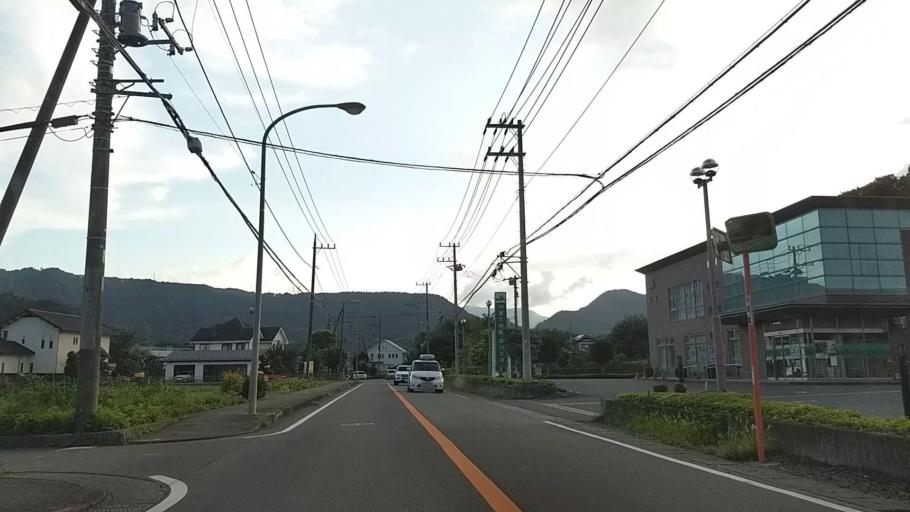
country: JP
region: Tokyo
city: Hachioji
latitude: 35.5683
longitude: 139.2613
